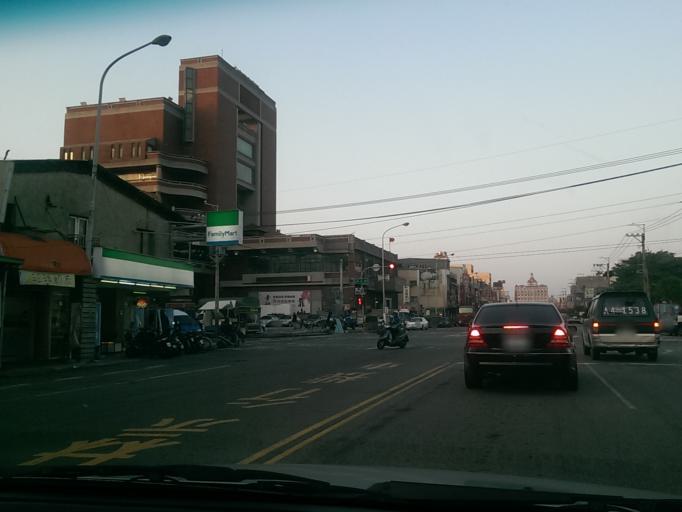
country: TW
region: Taiwan
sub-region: Changhua
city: Chang-hua
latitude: 24.2536
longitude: 120.5300
